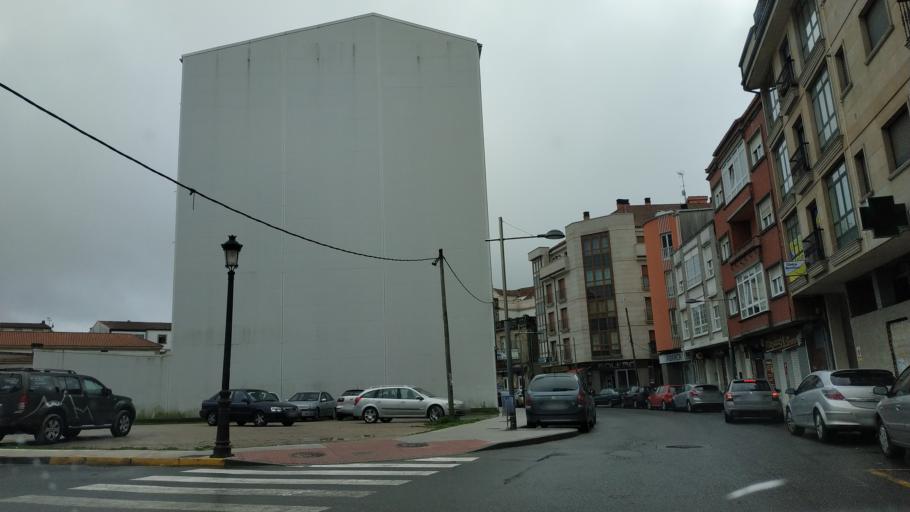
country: ES
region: Galicia
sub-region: Provincia da Coruna
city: Negreira
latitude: 42.9105
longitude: -8.7370
